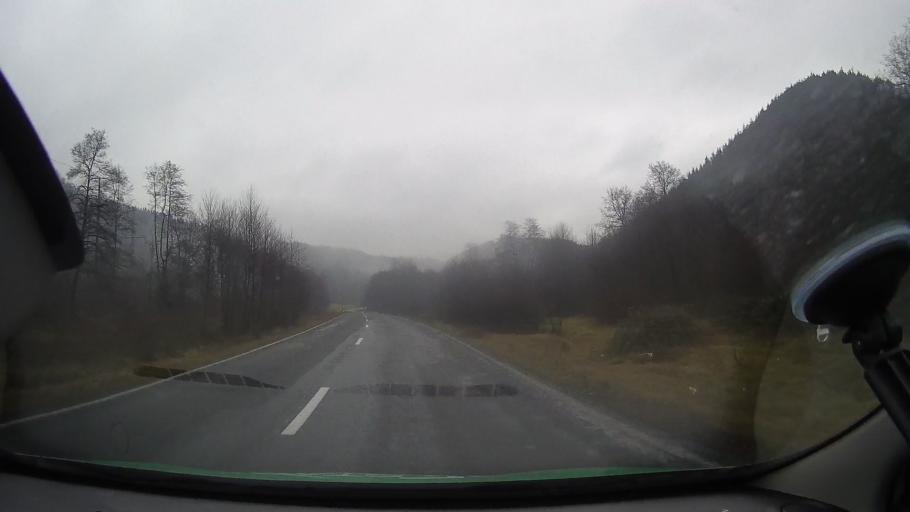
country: RO
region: Arad
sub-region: Comuna Plescuta
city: Plescuta
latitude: 46.3125
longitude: 22.4563
